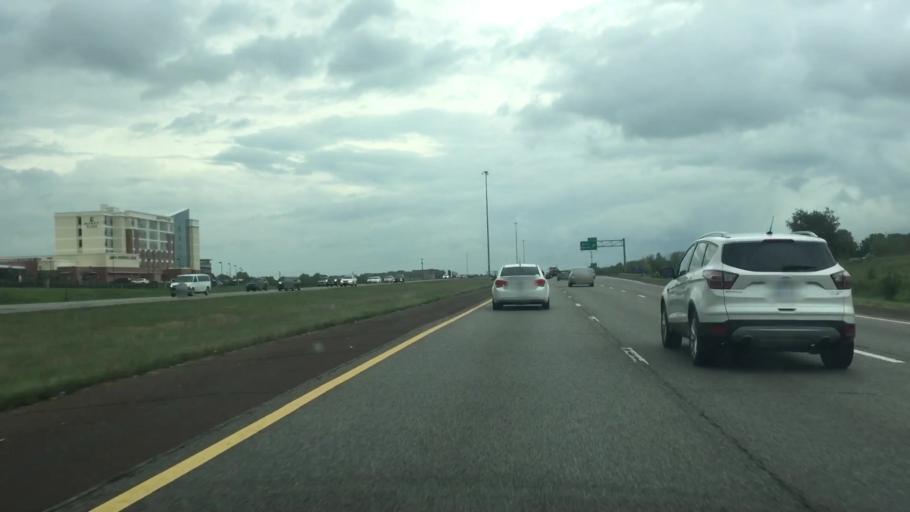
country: US
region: Kansas
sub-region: Johnson County
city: Lenexa
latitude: 38.9666
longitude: -94.7762
